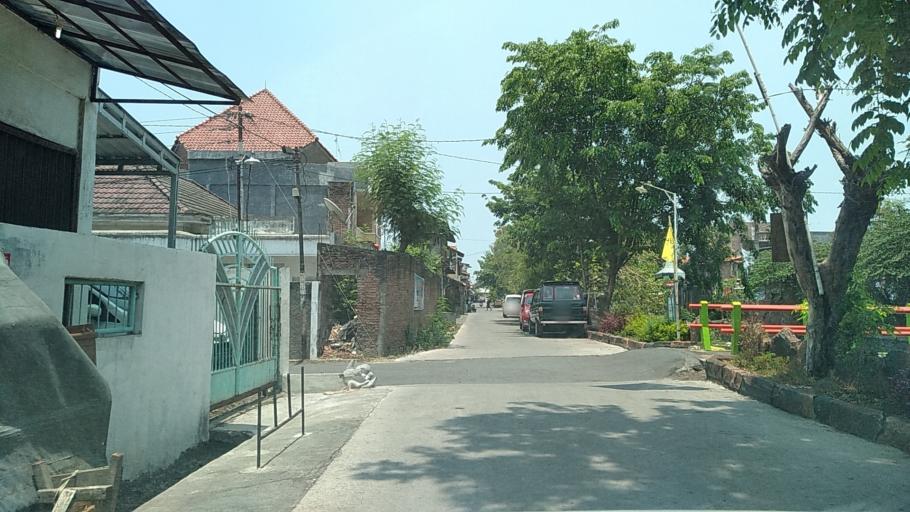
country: ID
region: Central Java
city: Semarang
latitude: -6.9769
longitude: 110.4373
